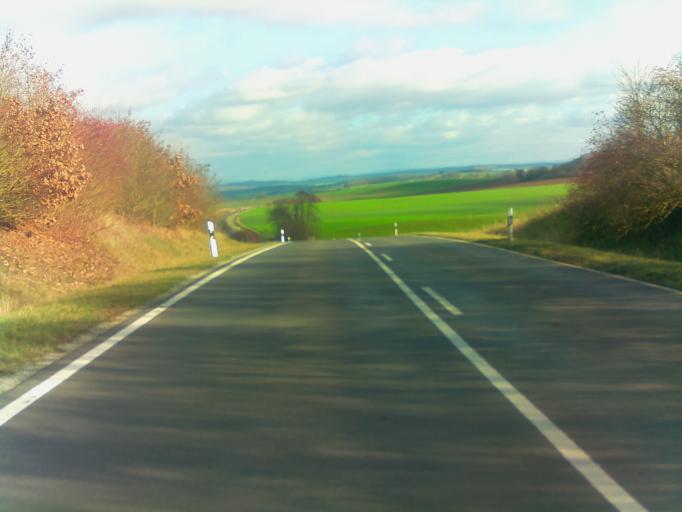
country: DE
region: Thuringia
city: Gleichamberg
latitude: 50.3476
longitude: 10.6085
